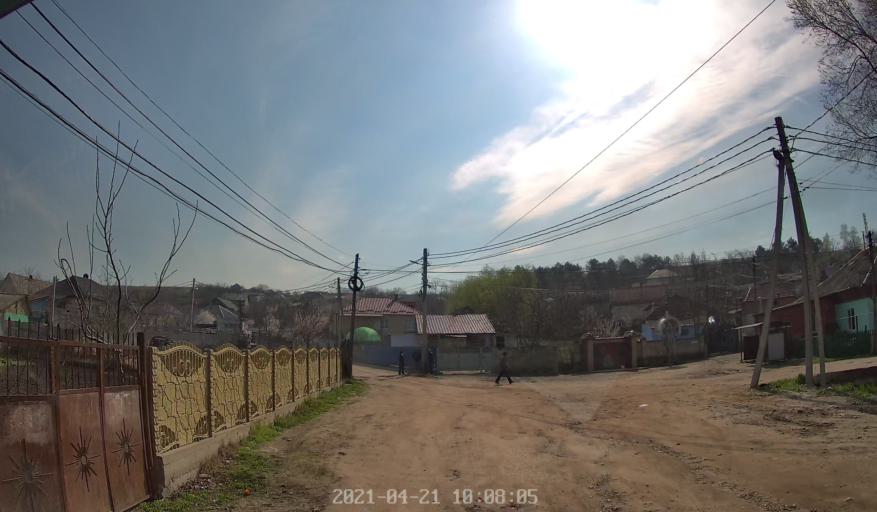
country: MD
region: Chisinau
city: Singera
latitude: 46.9845
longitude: 28.9455
